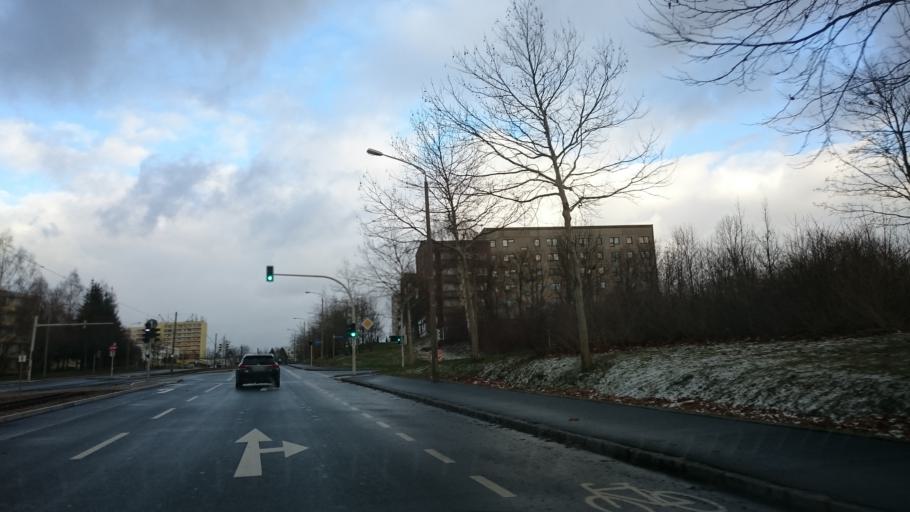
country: DE
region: Saxony
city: Zwickau
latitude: 50.7325
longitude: 12.5164
